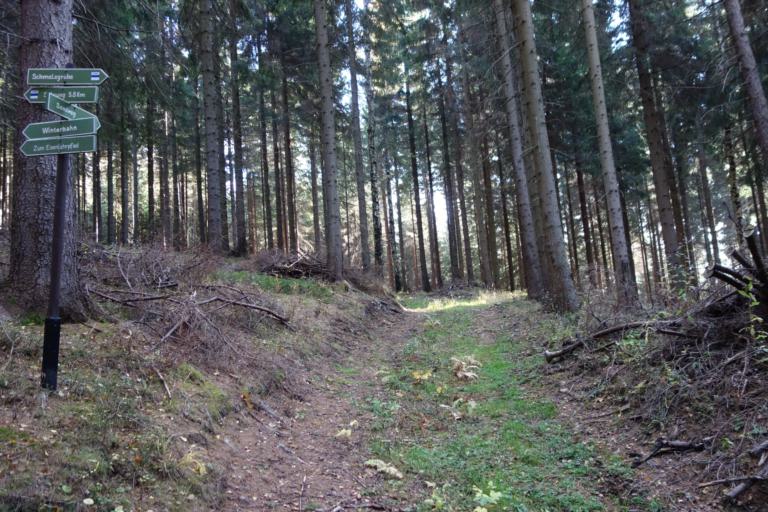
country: DE
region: Saxony
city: Johstadt
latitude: 50.5296
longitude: 13.1358
